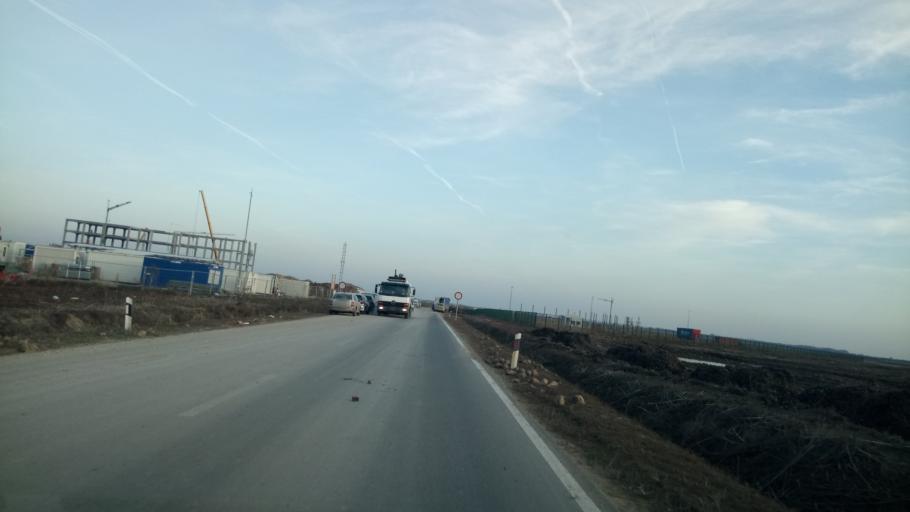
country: RS
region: Autonomna Pokrajina Vojvodina
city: Nova Pazova
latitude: 44.9622
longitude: 20.2369
